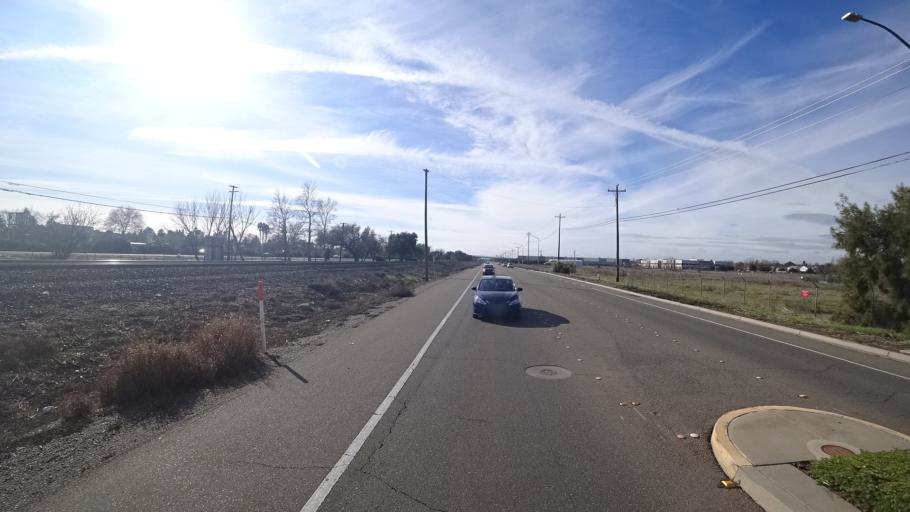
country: US
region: California
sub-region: Yolo County
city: Davis
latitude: 38.5526
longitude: -121.6996
